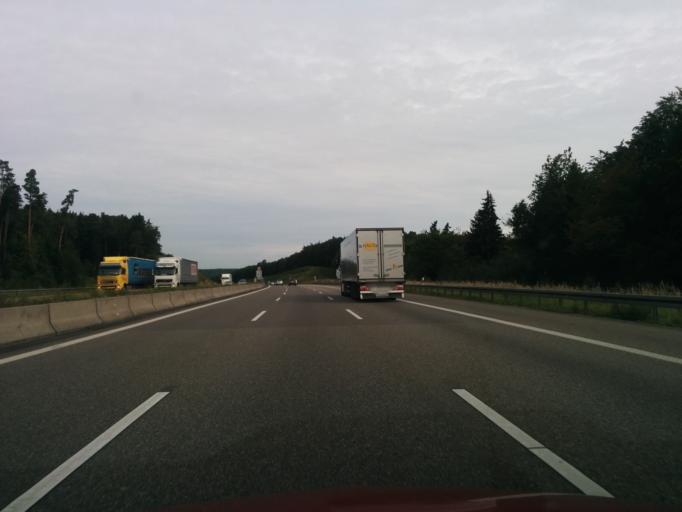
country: DE
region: Baden-Wuerttemberg
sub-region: Karlsruhe Region
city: Niefern-Oschelbronn
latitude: 48.8933
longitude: 8.7858
